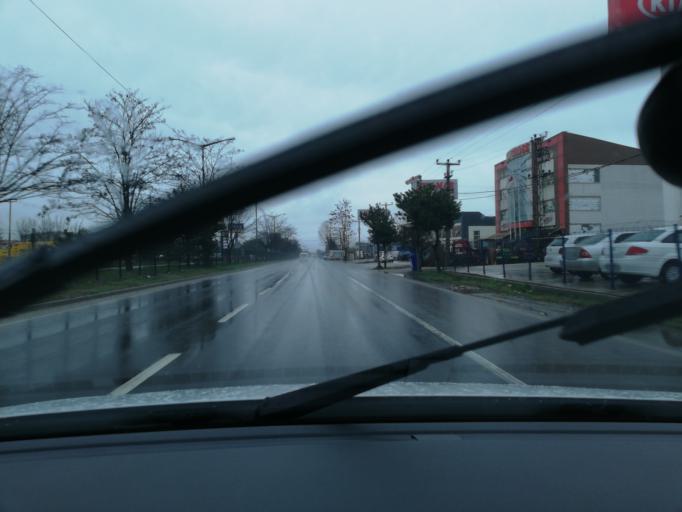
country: TR
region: Bolu
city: Bolu
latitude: 40.7357
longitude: 31.6421
